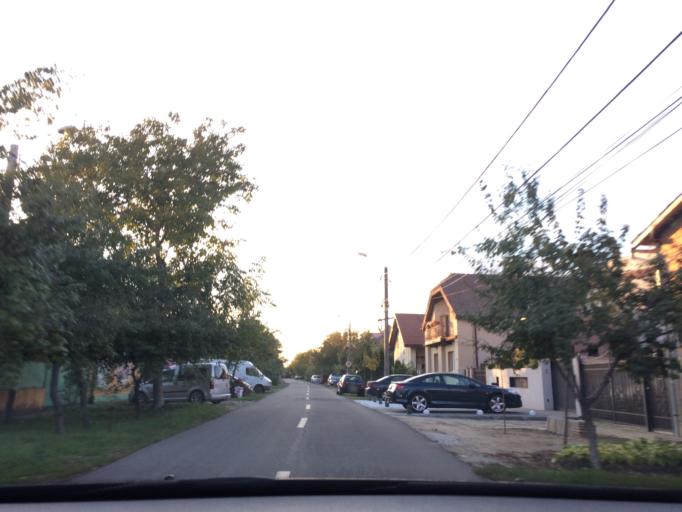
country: RO
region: Timis
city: Timisoara
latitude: 45.7652
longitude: 21.1987
